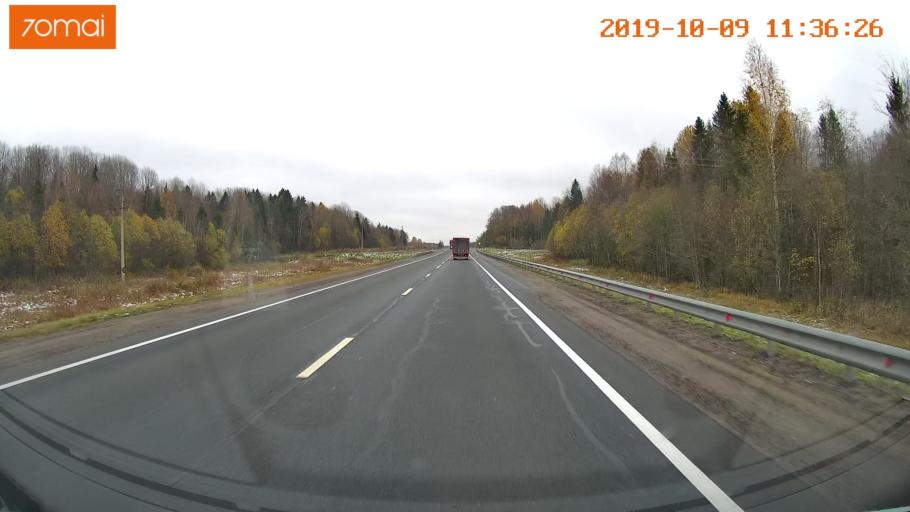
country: RU
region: Vologda
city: Gryazovets
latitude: 58.9906
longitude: 40.1368
